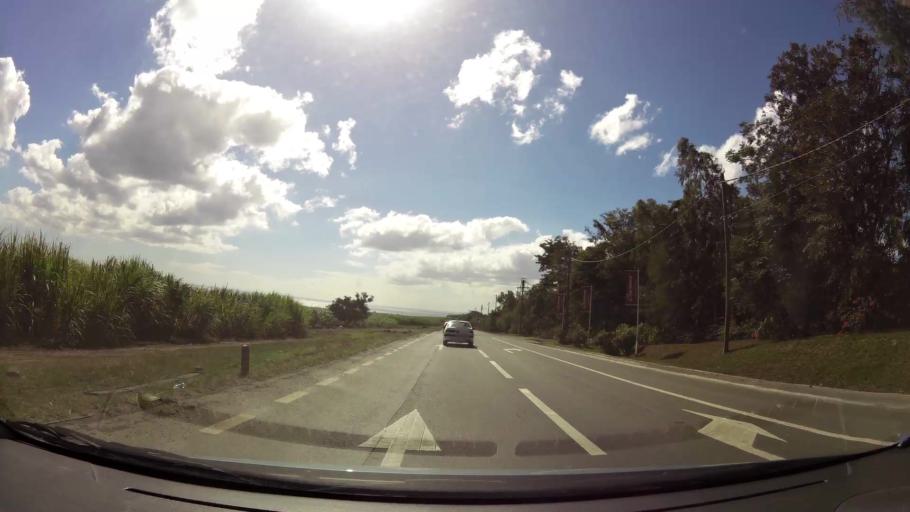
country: MU
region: Black River
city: Gros Cailloux
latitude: -20.2343
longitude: 57.4253
